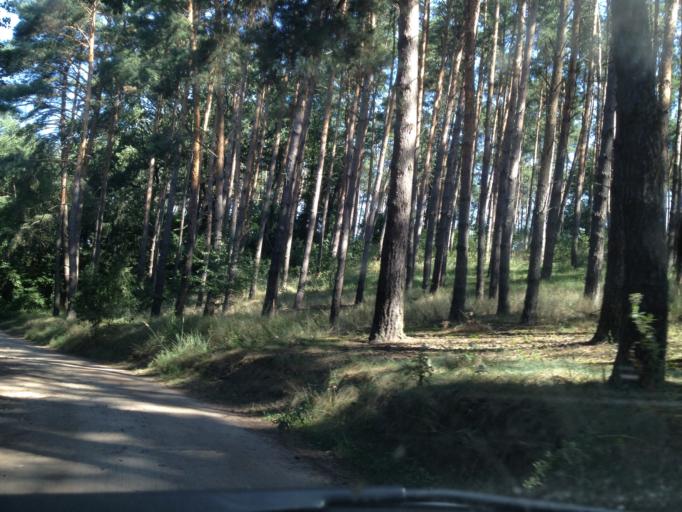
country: PL
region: Greater Poland Voivodeship
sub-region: Powiat sredzki
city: Zaniemysl
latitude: 52.1039
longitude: 17.1322
